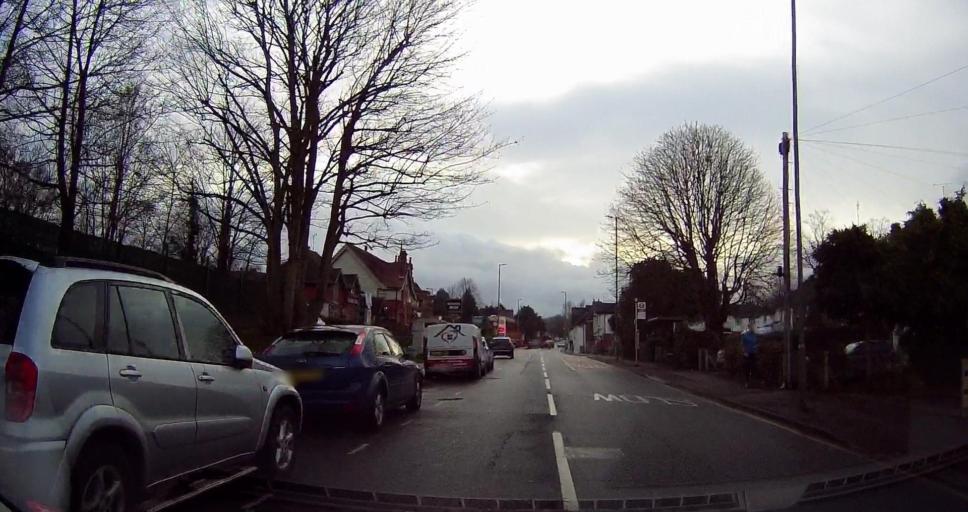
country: GB
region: England
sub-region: Greater London
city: Orpington
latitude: 51.3532
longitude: 0.0898
